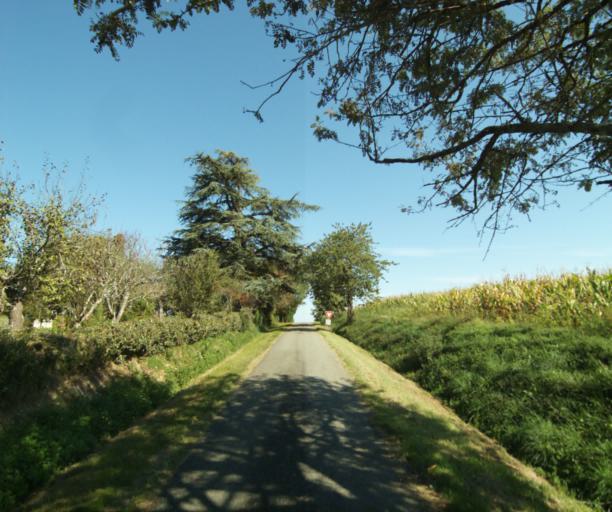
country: FR
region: Aquitaine
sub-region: Departement des Landes
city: Gabarret
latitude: 43.9486
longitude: 0.0037
